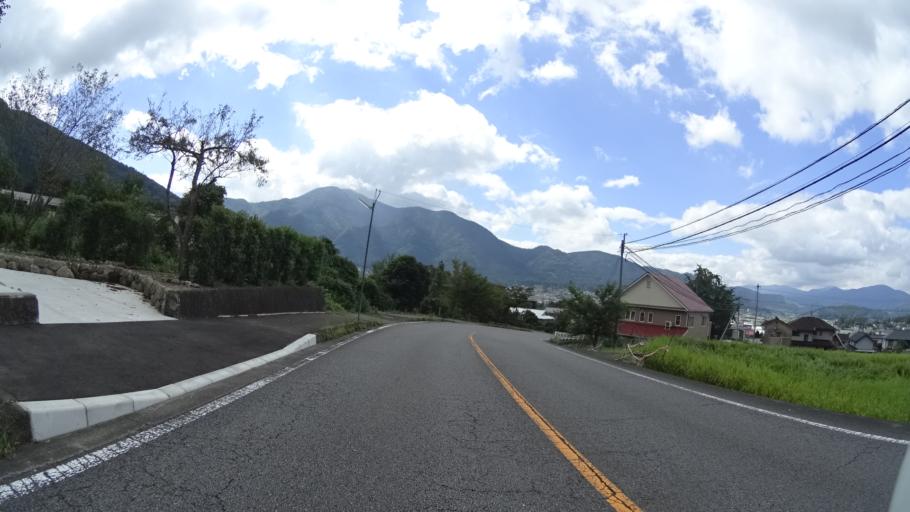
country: JP
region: Oita
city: Beppu
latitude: 33.2735
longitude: 131.3640
